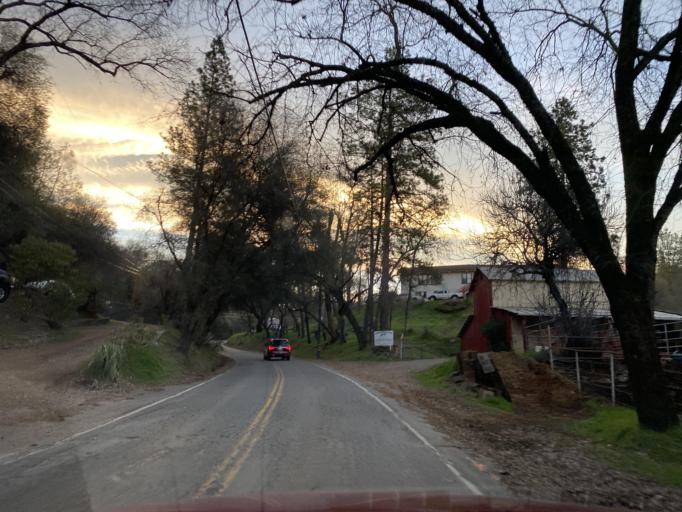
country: US
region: California
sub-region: Amador County
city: Plymouth
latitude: 38.5029
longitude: -120.7528
